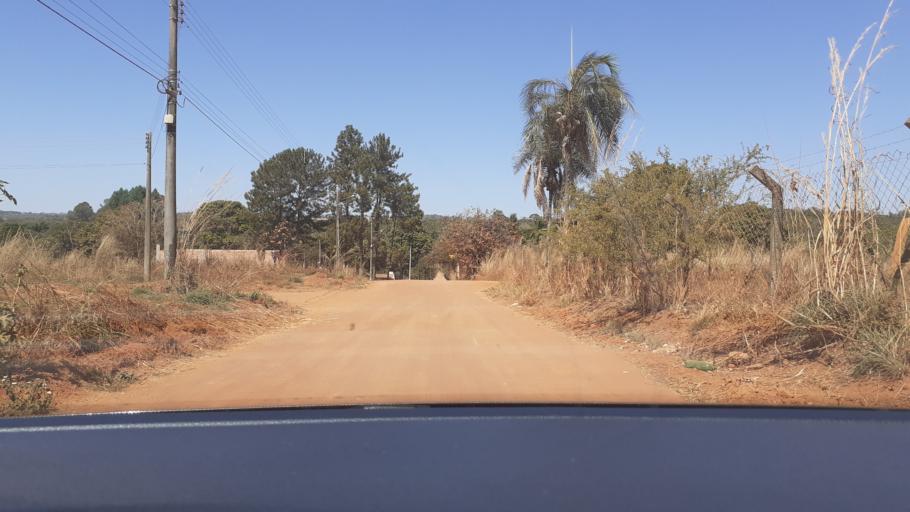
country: BR
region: Goias
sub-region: Aparecida De Goiania
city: Aparecida de Goiania
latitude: -16.8764
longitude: -49.2772
